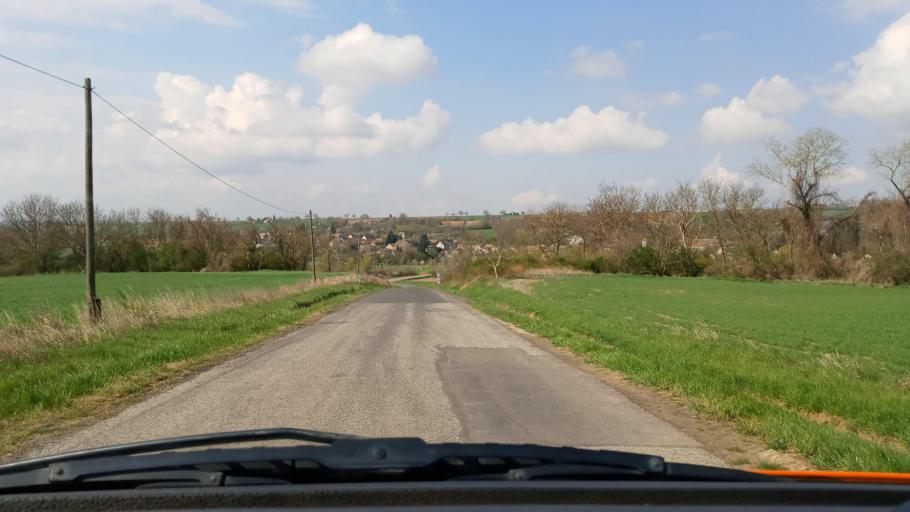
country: HU
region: Baranya
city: Pecsvarad
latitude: 46.1036
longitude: 18.4802
